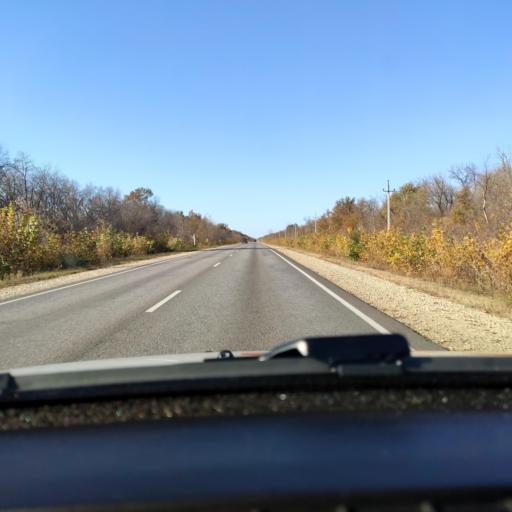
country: RU
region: Voronezj
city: Latnaya
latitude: 51.8062
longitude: 38.8622
